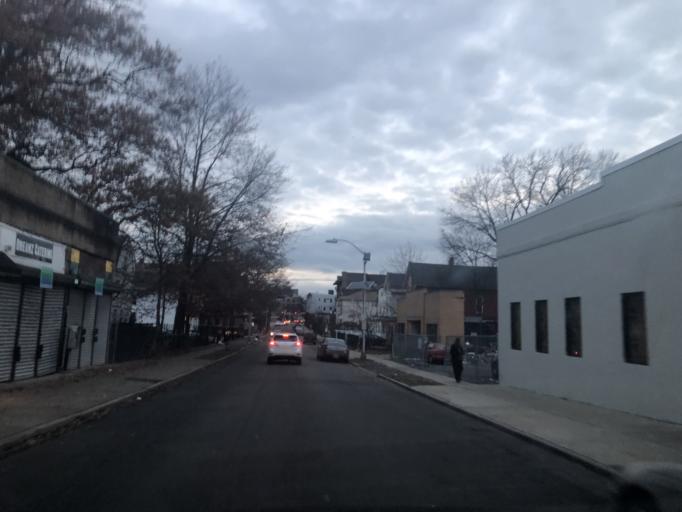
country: US
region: New Jersey
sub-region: Essex County
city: East Orange
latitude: 40.7656
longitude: -74.2130
